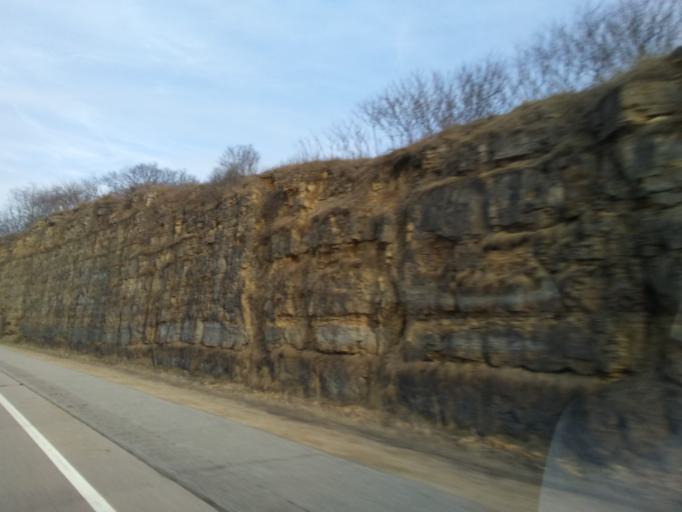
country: US
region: Wisconsin
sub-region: Iowa County
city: Barneveld
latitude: 42.9959
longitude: -89.9870
